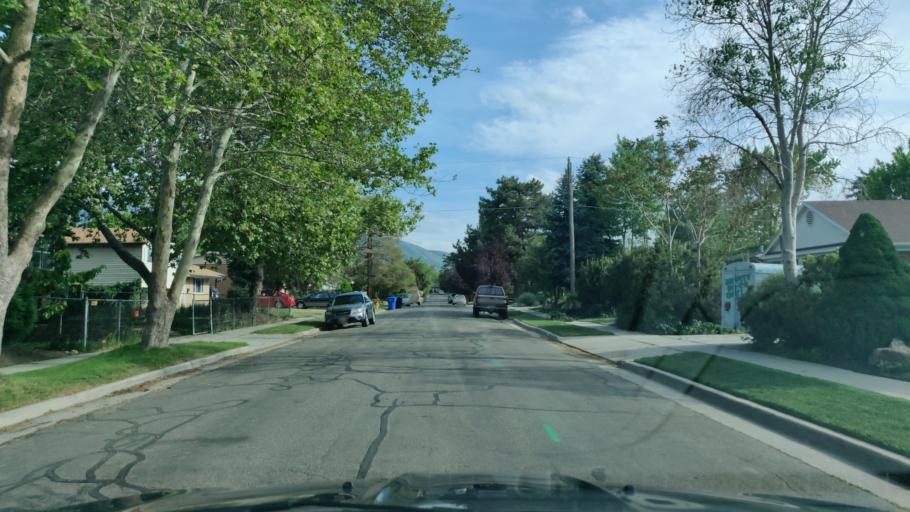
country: US
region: Utah
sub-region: Salt Lake County
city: Cottonwood Heights
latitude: 40.6207
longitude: -111.8134
